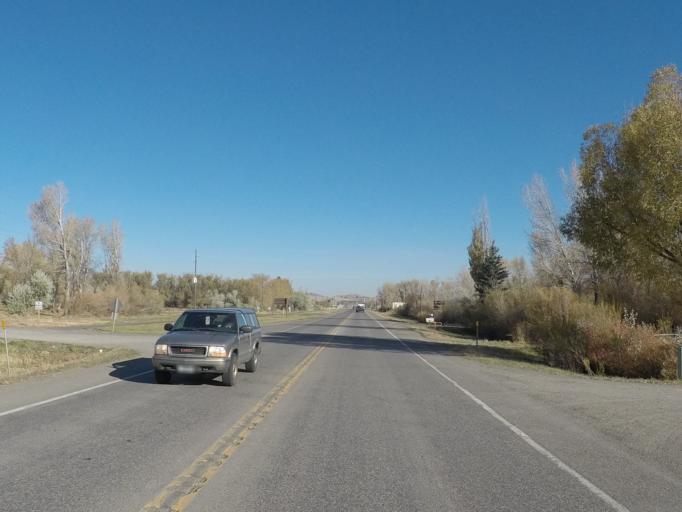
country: US
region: Montana
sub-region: Park County
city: Livingston
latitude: 45.6263
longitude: -110.5775
